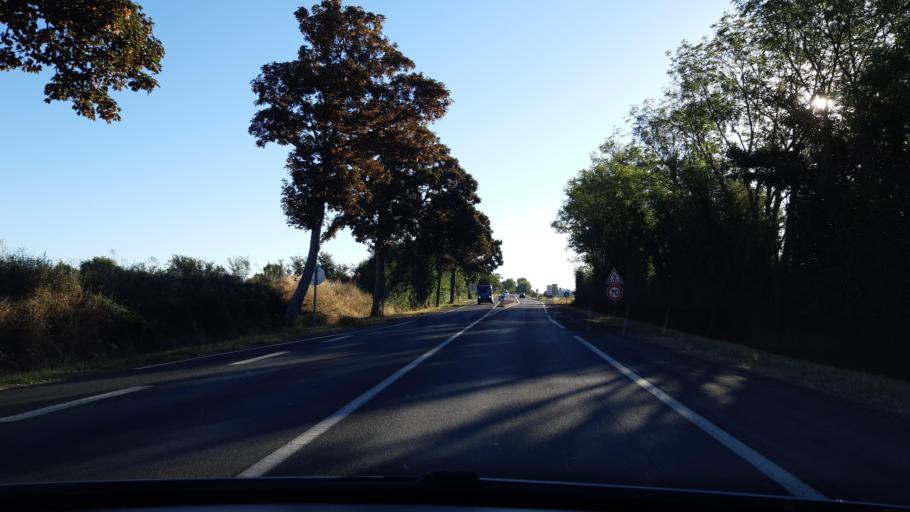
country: FR
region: Poitou-Charentes
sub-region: Departement des Deux-Sevres
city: Azay-le-Brule
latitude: 46.3970
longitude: -0.2458
